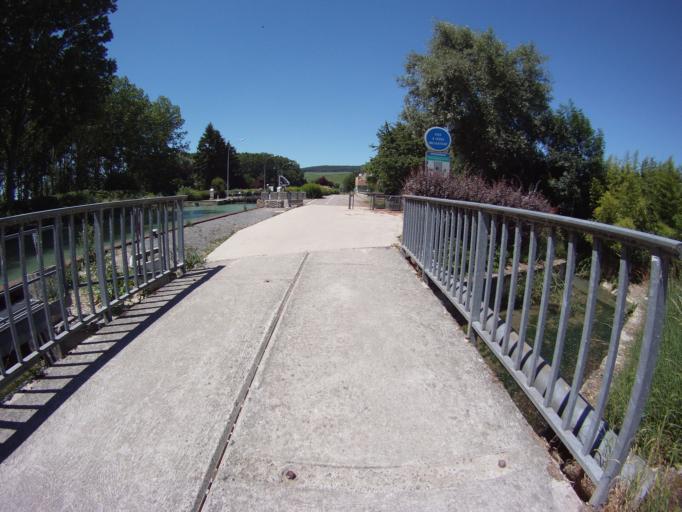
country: FR
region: Champagne-Ardenne
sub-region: Departement de la Marne
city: Epernay
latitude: 49.0699
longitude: 3.9450
